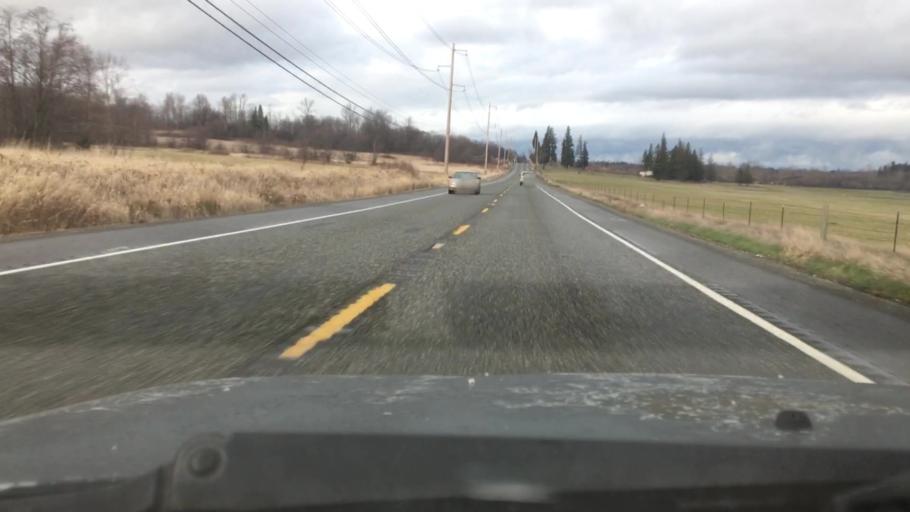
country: US
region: Washington
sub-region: Whatcom County
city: Ferndale
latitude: 48.8359
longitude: -122.6824
